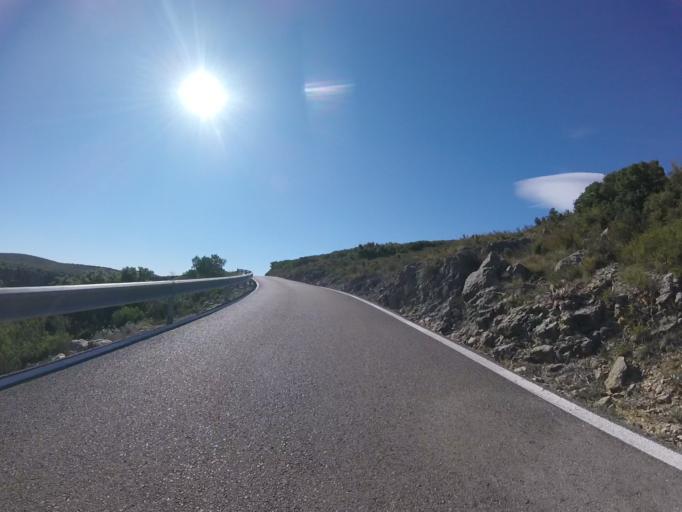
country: ES
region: Valencia
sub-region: Provincia de Castello
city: Albocasser
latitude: 40.3933
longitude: 0.0400
